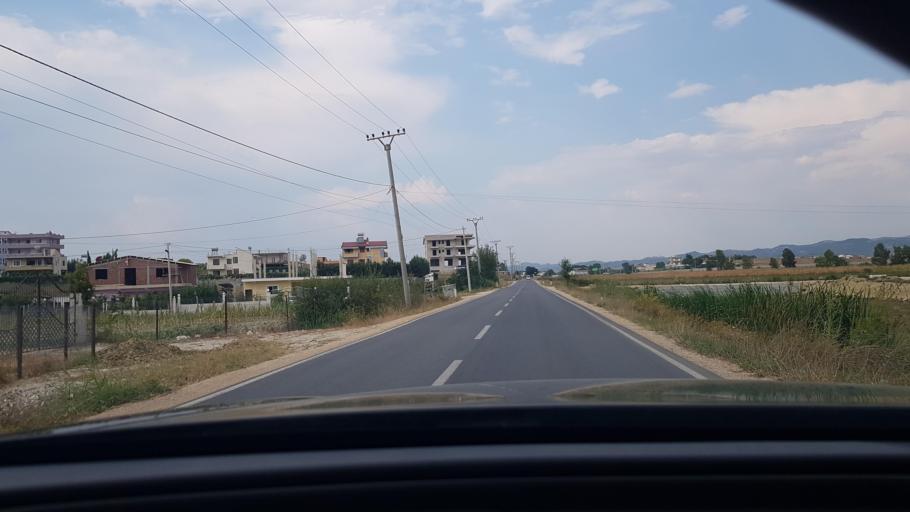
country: AL
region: Durres
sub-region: Rrethi i Durresit
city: Katundi i Ri
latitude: 41.4157
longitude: 19.5459
